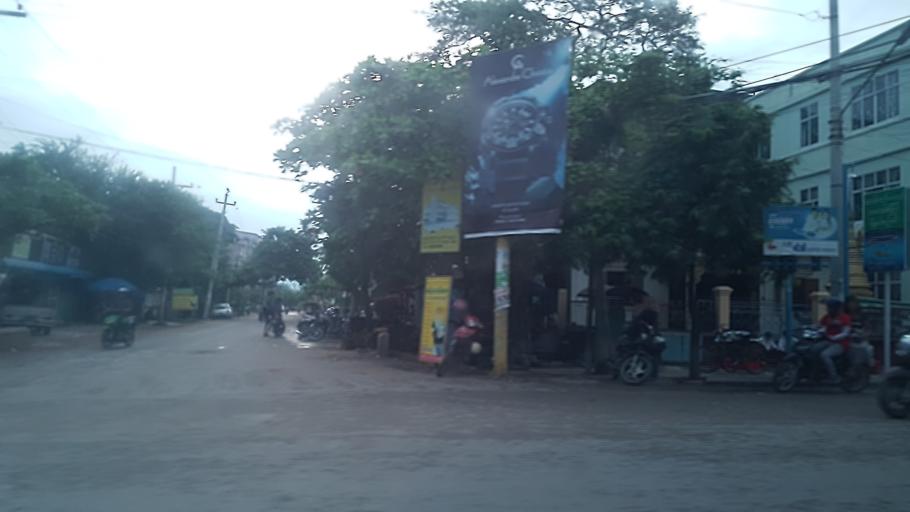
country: MM
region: Mandalay
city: Mandalay
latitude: 21.9641
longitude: 96.0948
